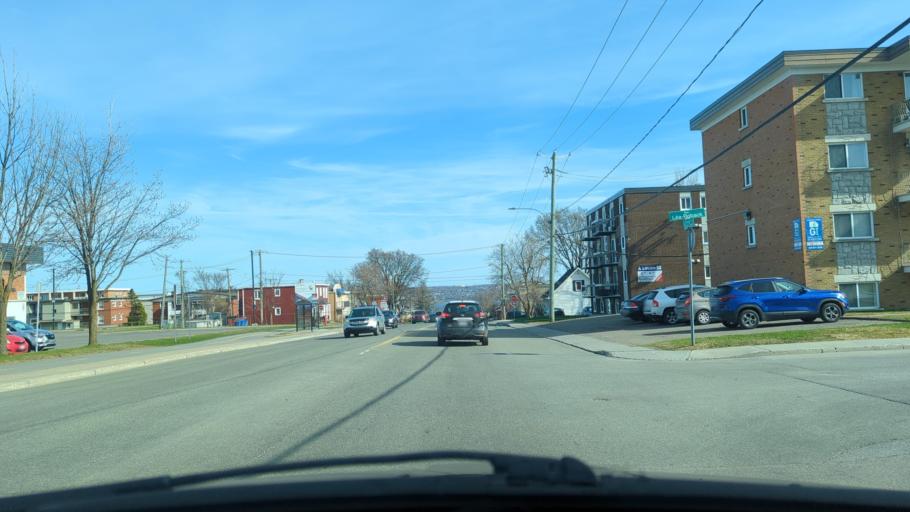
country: CA
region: Quebec
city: Quebec
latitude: 46.8598
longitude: -71.2107
